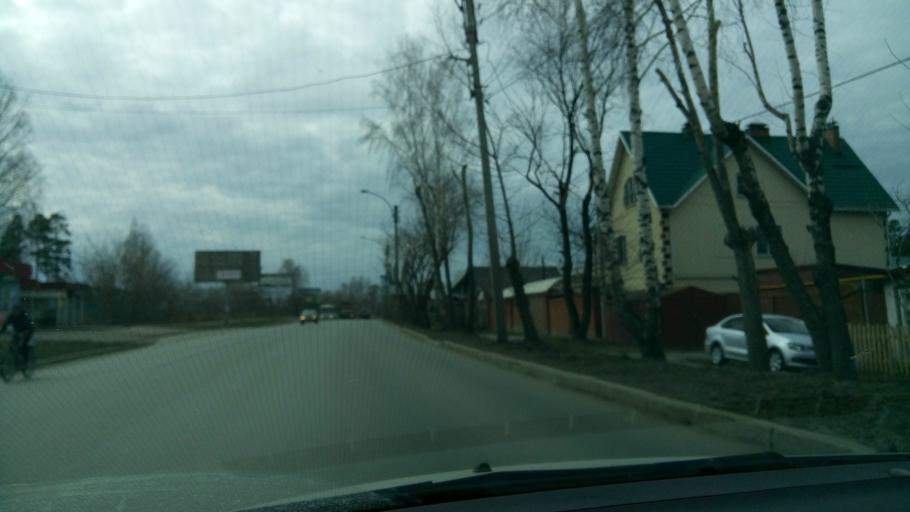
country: RU
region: Sverdlovsk
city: Beryozovsky
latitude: 56.8857
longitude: 60.7247
